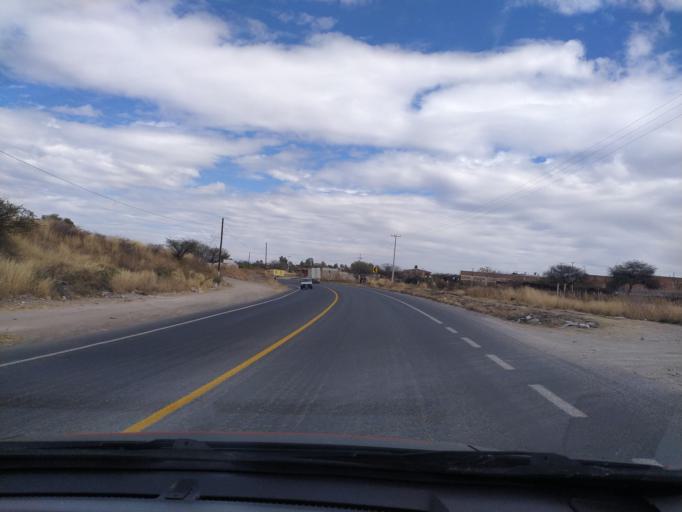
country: LA
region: Oudomxai
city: Muang La
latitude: 20.9936
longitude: 101.8382
